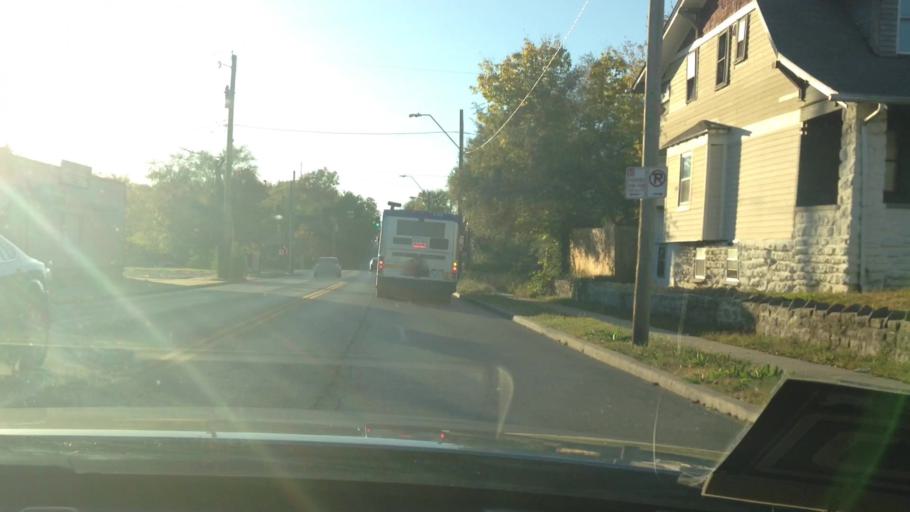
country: US
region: Missouri
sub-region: Jackson County
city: Kansas City
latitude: 39.0559
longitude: -94.5662
